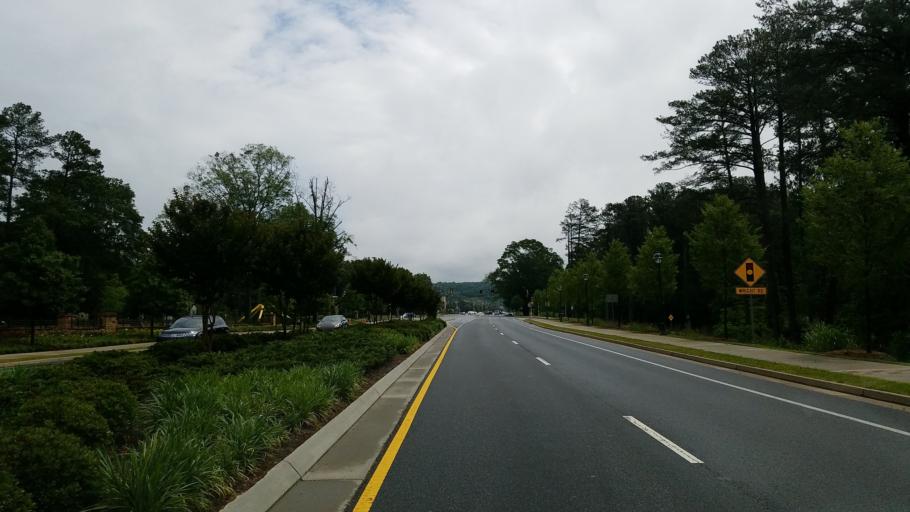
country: US
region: Georgia
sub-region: Fulton County
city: Sandy Springs
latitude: 33.9363
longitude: -84.3846
